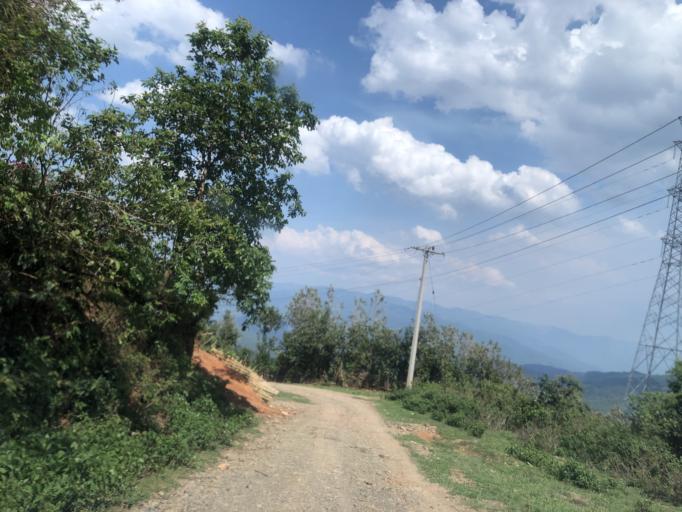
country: LA
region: Phongsali
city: Phongsali
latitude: 21.4121
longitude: 102.2457
